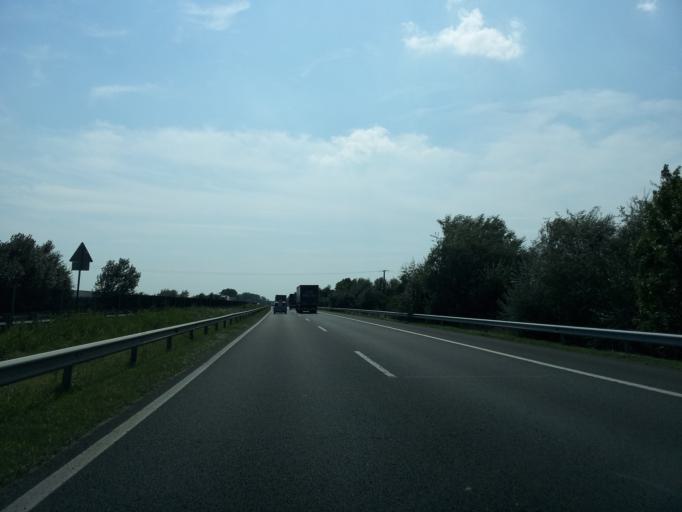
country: HU
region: Fejer
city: Baracska
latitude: 47.2824
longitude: 18.7118
